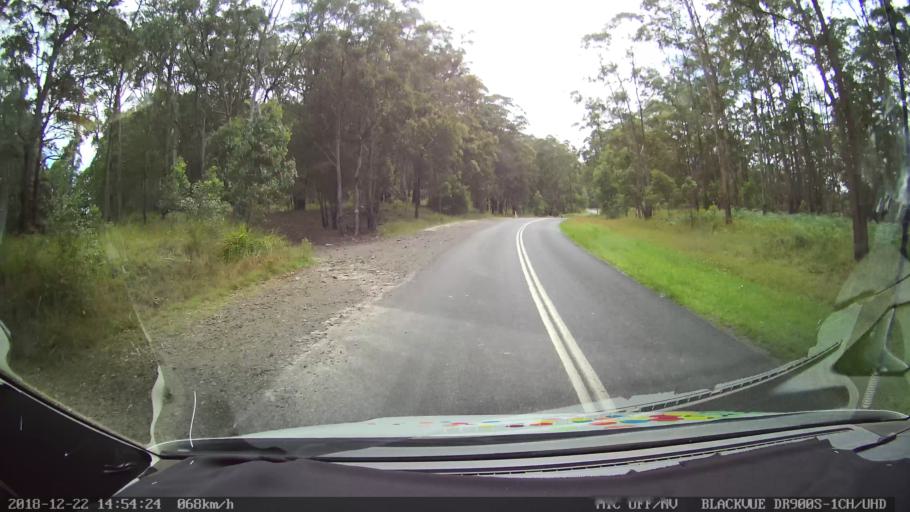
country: AU
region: New South Wales
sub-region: Bellingen
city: Dorrigo
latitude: -30.2262
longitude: 152.5331
